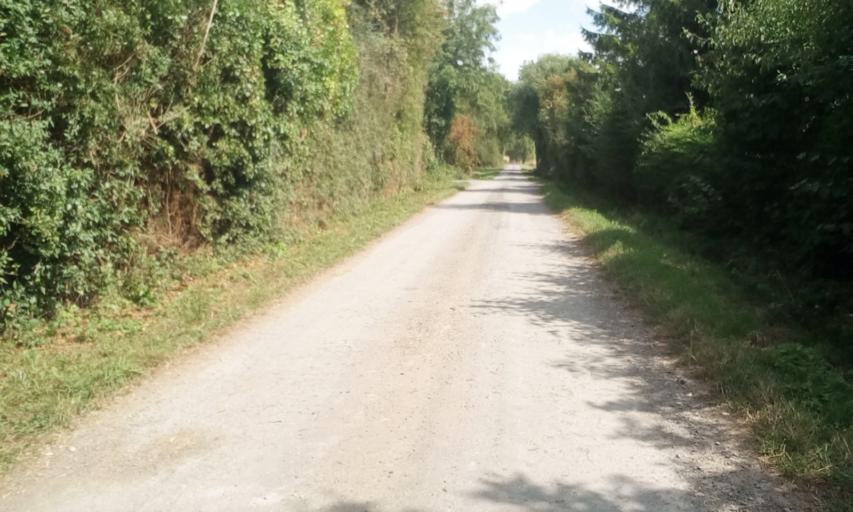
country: FR
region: Lower Normandy
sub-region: Departement du Calvados
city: Argences
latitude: 49.1344
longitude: -0.1775
